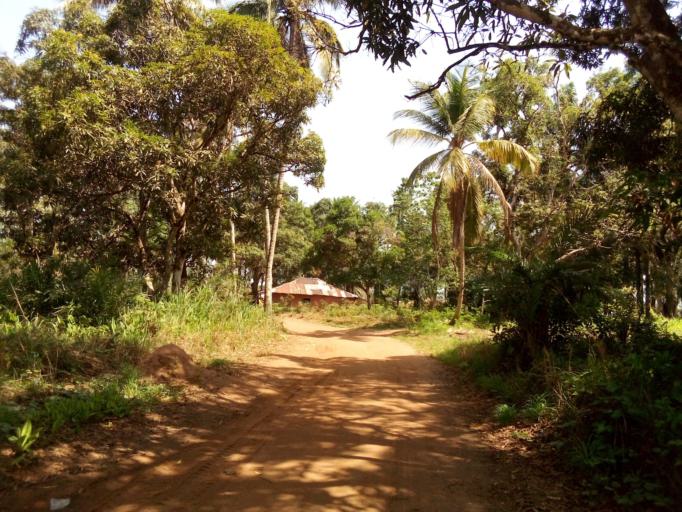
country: SL
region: Western Area
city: Waterloo
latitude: 8.3411
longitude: -13.0098
